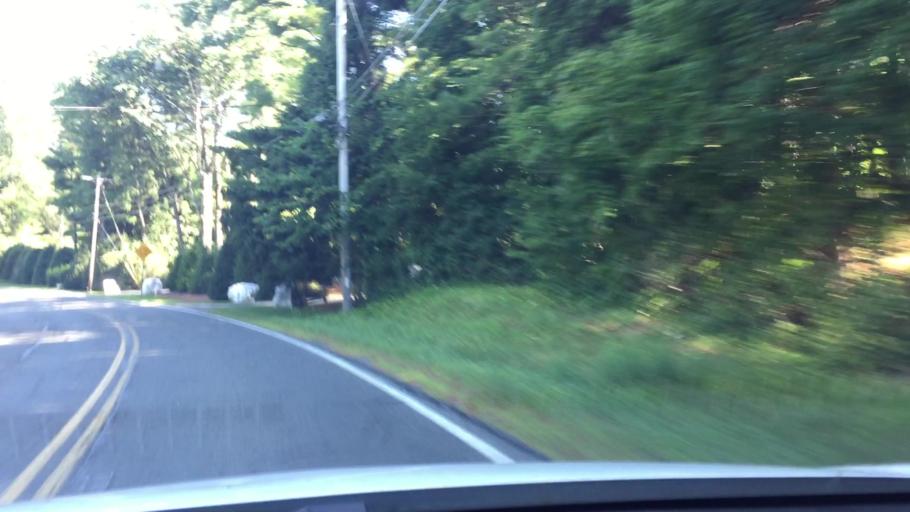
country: US
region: Massachusetts
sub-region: Berkshire County
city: West Stockbridge
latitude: 42.3121
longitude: -73.3697
